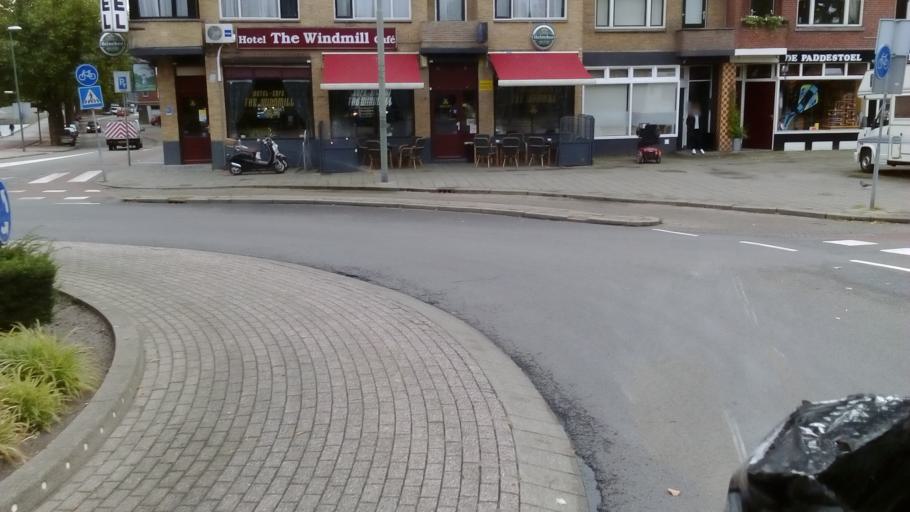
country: NL
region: South Holland
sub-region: Gemeente Schiedam
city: Schiedam
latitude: 51.9173
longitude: 4.3919
